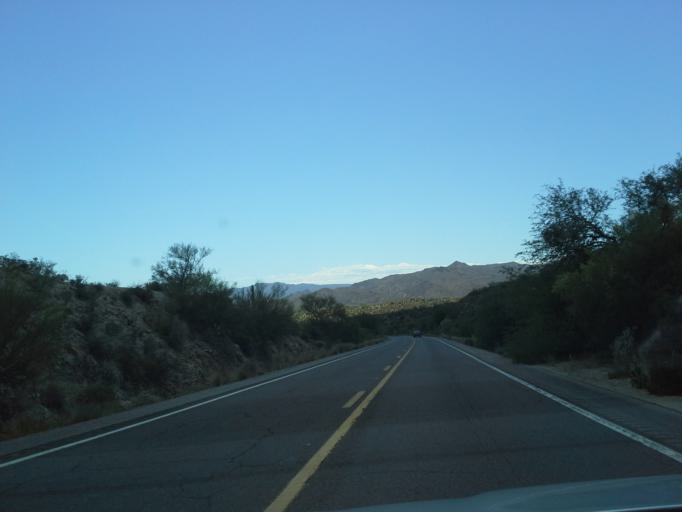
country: US
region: Arizona
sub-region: Pinal County
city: Kearny
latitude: 33.1393
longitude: -110.9902
